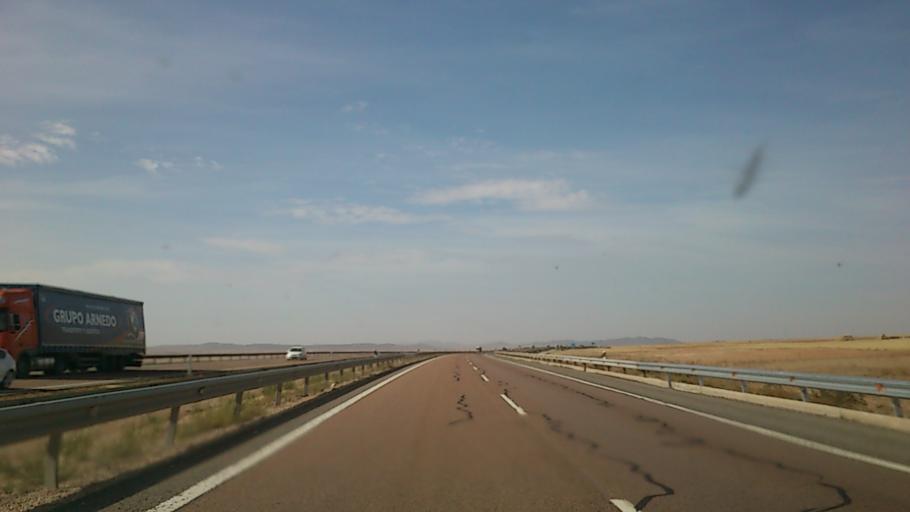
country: ES
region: Aragon
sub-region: Provincia de Teruel
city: Villafranca del Campo
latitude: 40.7171
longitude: -1.3242
